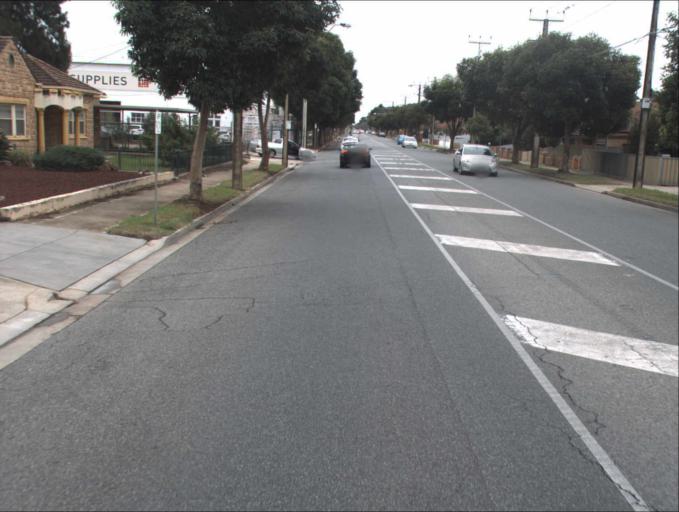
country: AU
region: South Australia
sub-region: Charles Sturt
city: Woodville
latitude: -34.8797
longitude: 138.5665
